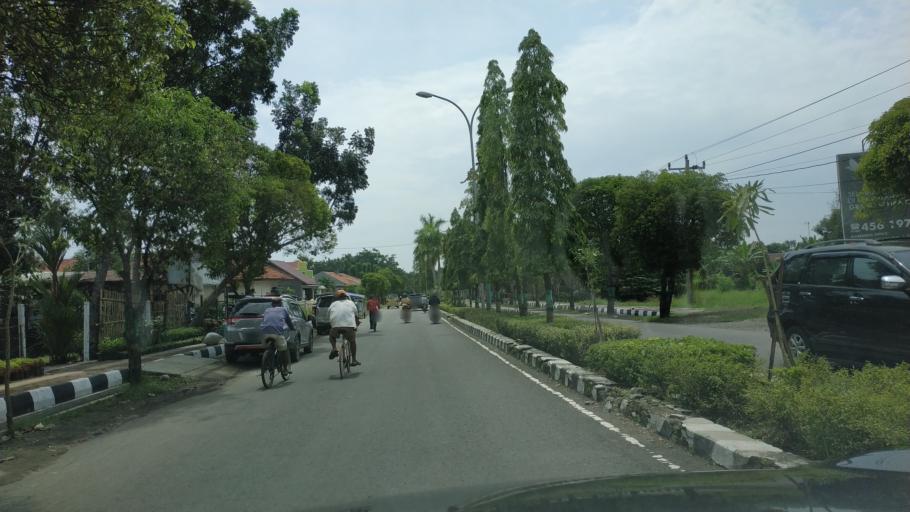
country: ID
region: Central Java
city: Slawi
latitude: -6.9896
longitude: 109.1275
